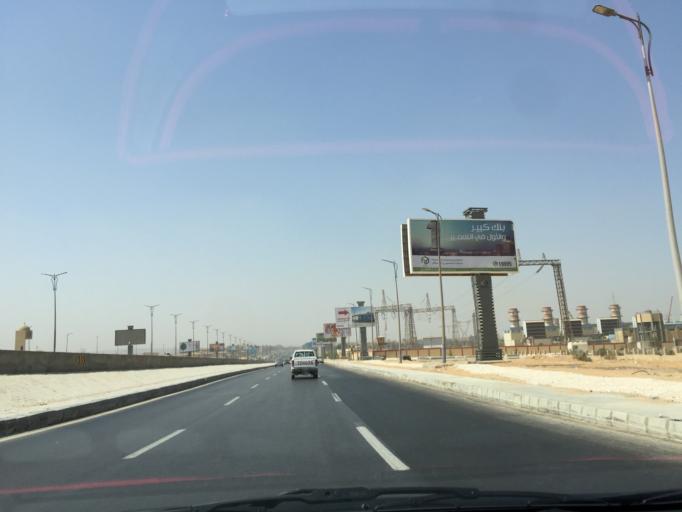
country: EG
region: Al Jizah
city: Awsim
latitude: 30.0498
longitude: 31.0485
